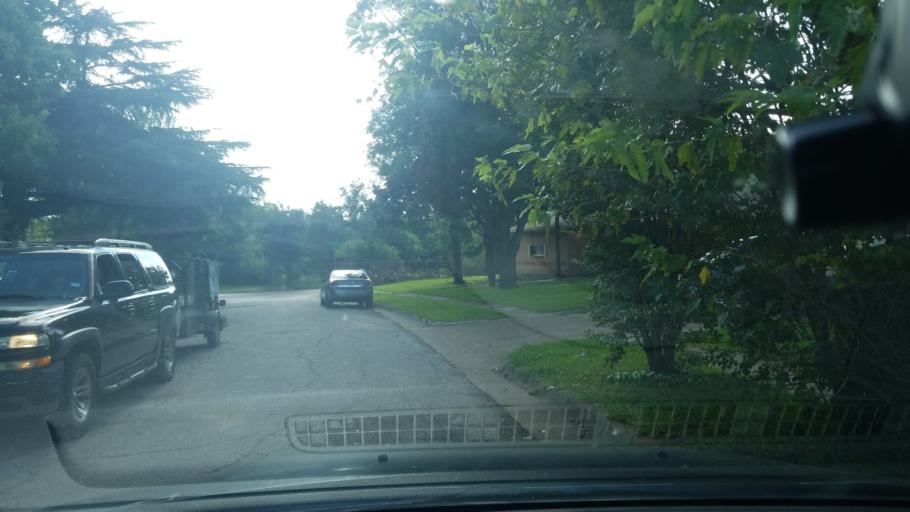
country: US
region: Texas
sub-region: Dallas County
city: Balch Springs
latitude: 32.7420
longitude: -96.6641
